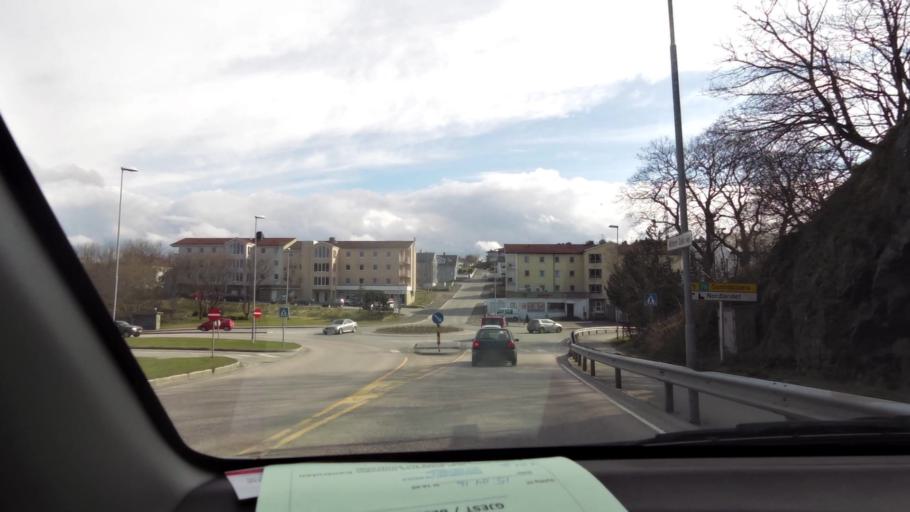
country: NO
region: More og Romsdal
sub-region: Kristiansund
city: Kristiansund
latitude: 63.0474
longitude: 7.7199
